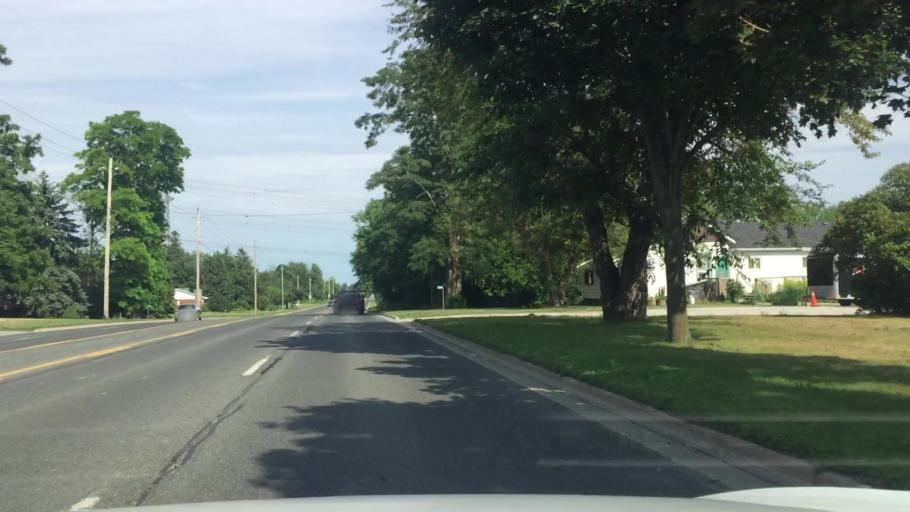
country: CA
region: Ontario
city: Oshawa
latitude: 43.9137
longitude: -78.7442
